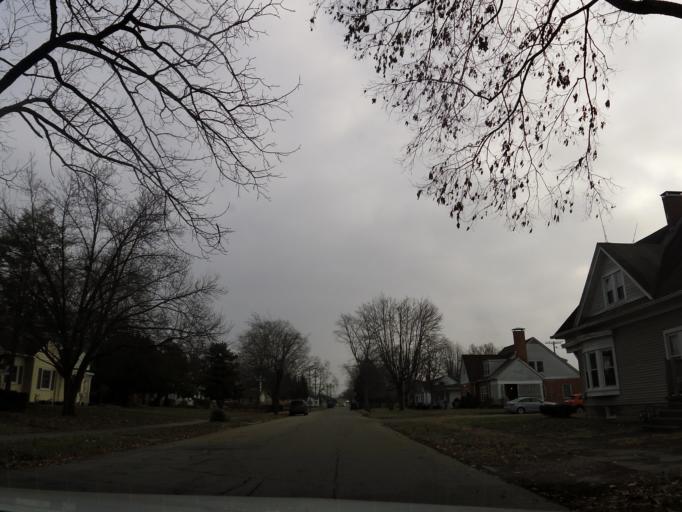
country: US
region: Indiana
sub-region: Bartholomew County
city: Columbus
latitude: 39.2147
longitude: -85.9108
